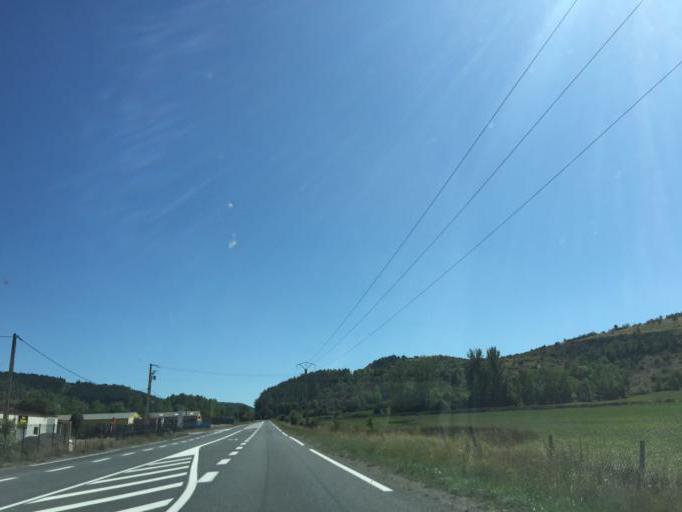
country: FR
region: Midi-Pyrenees
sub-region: Departement de l'Aveyron
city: Saint-Georges-de-Luzencon
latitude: 43.9909
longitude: 2.9673
